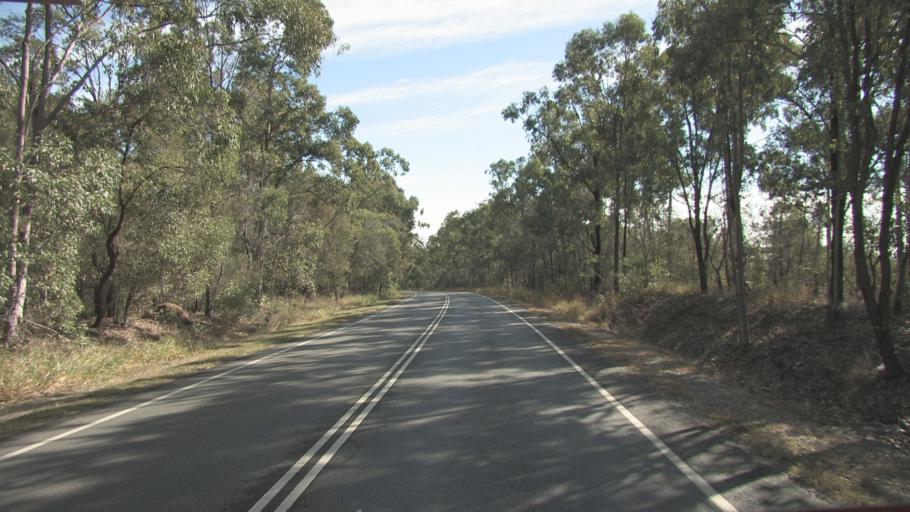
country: AU
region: Queensland
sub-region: Brisbane
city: Forest Lake
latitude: -27.6410
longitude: 152.9744
